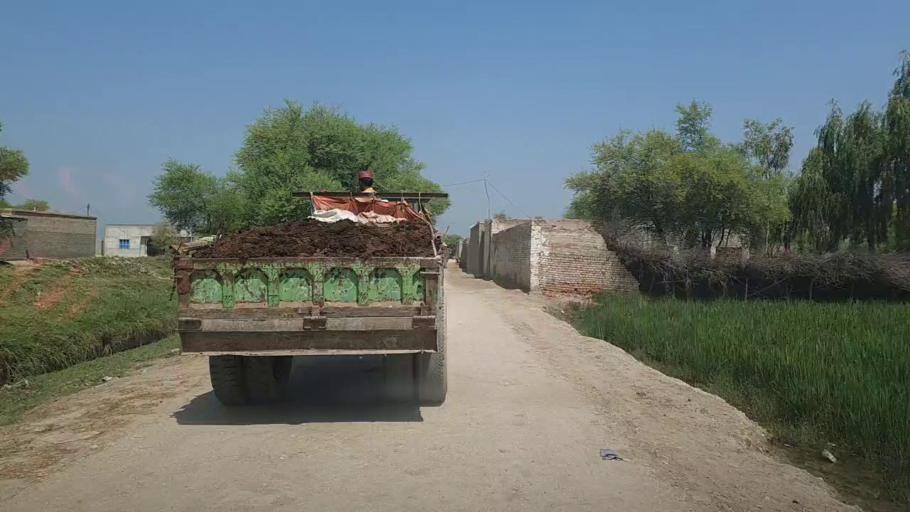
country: PK
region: Sindh
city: Kandhkot
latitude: 28.2955
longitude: 69.2924
